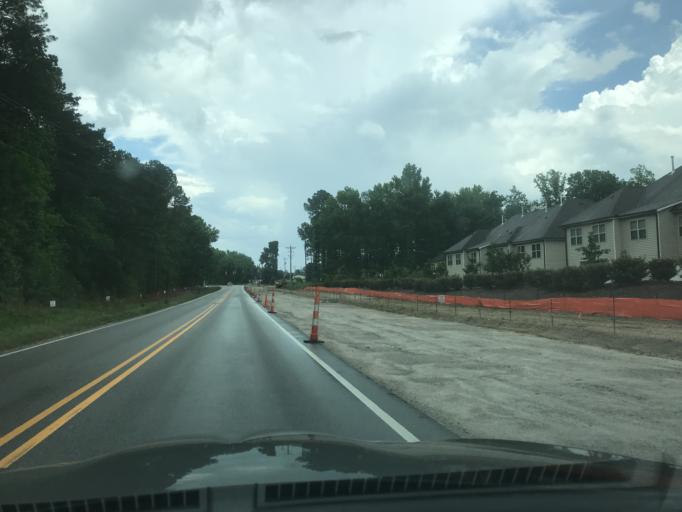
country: US
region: North Carolina
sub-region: Wake County
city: Knightdale
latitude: 35.8402
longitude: -78.5039
